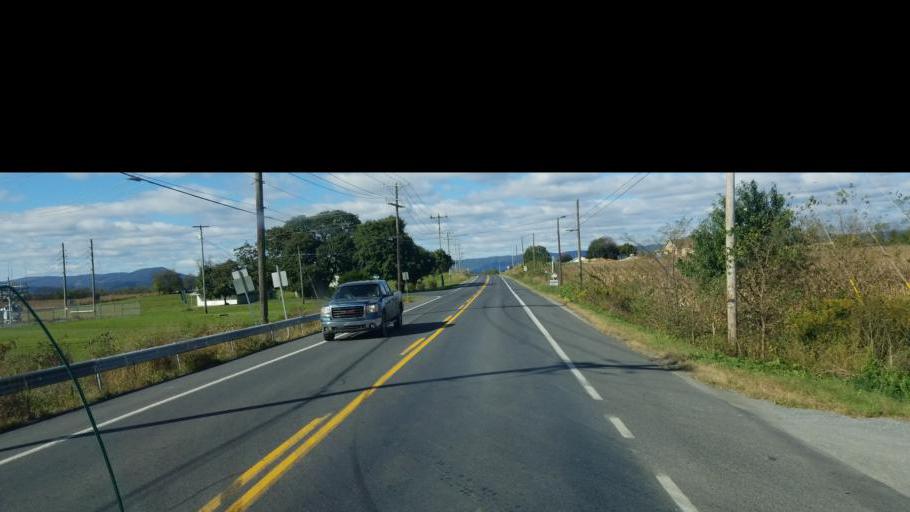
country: US
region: Pennsylvania
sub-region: Franklin County
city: Mercersburg
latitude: 39.8047
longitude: -77.8190
